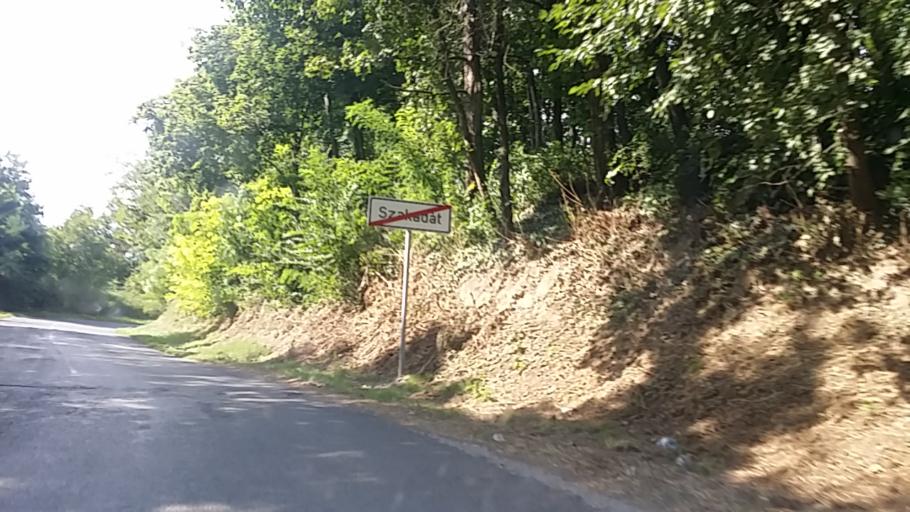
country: HU
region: Tolna
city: Gyonk
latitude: 46.5382
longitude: 18.4759
